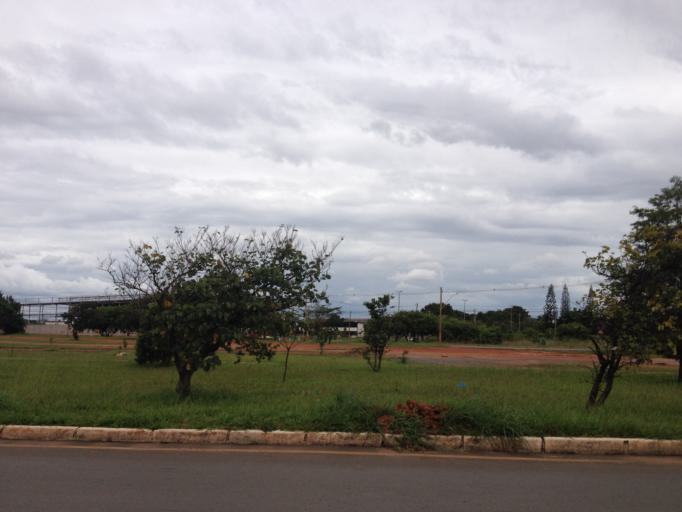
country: BR
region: Federal District
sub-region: Brasilia
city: Brasilia
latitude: -15.7915
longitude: -47.9796
